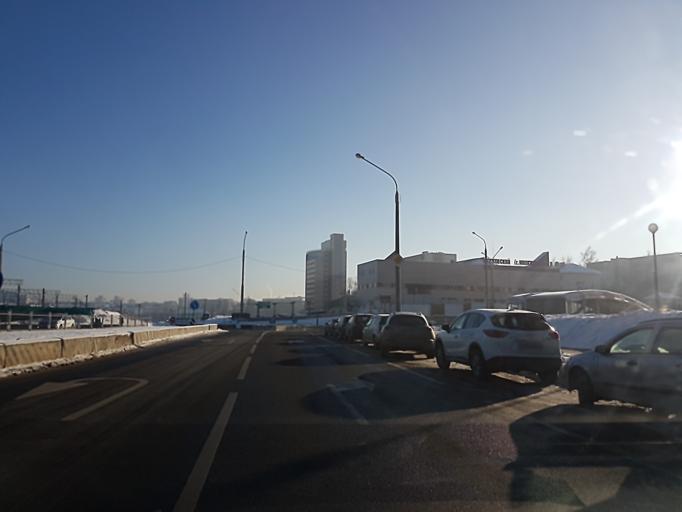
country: BY
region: Minsk
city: Minsk
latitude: 53.8976
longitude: 27.5295
